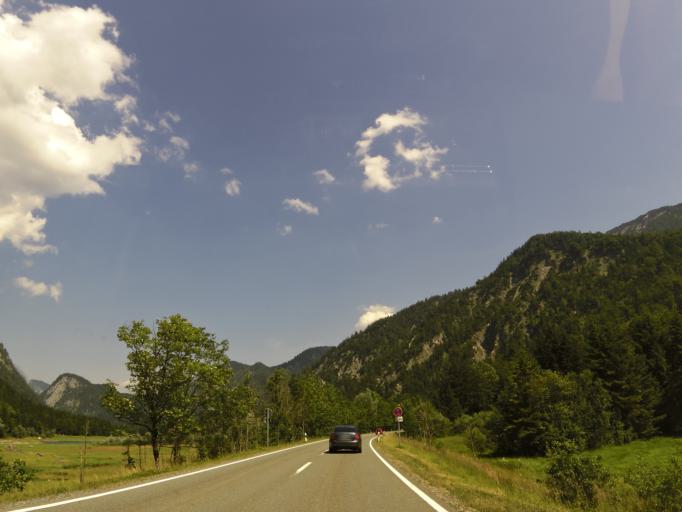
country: AT
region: Tyrol
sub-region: Politischer Bezirk Kitzbuhel
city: Waidring
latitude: 47.6887
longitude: 12.5768
